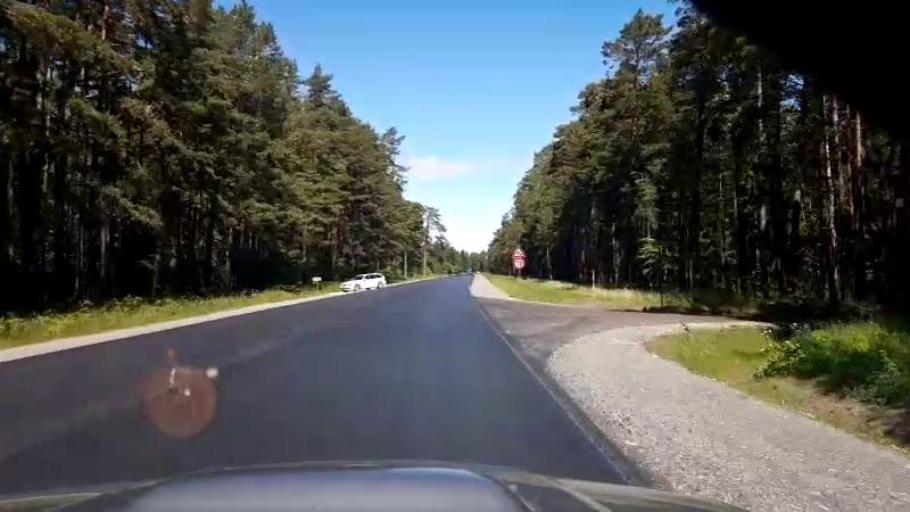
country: LV
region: Salacgrivas
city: Ainazi
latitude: 57.8287
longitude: 24.3446
